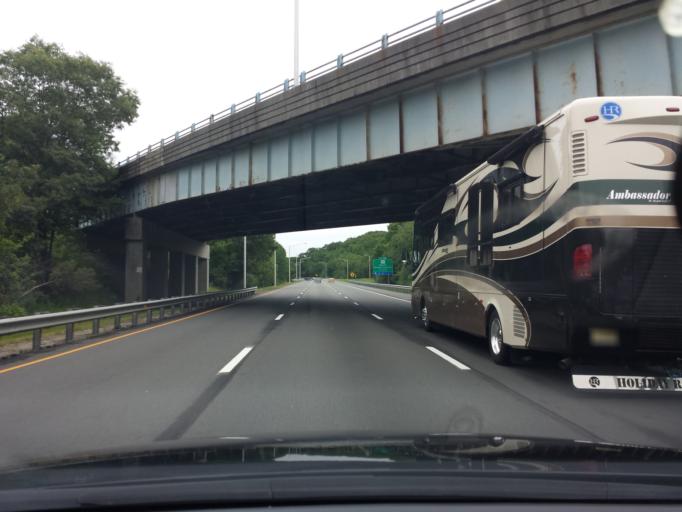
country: US
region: Connecticut
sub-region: New London County
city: Long Hill
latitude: 41.3610
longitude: -72.0563
